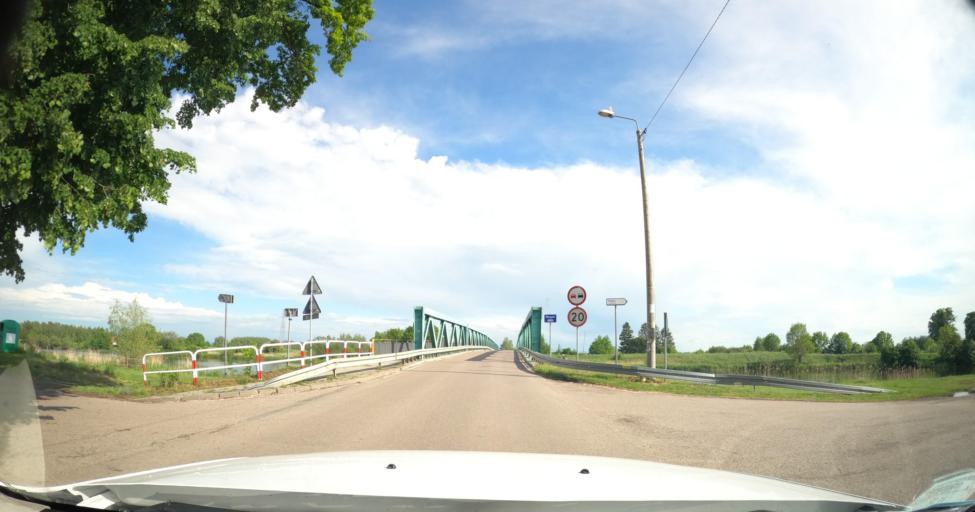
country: PL
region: Warmian-Masurian Voivodeship
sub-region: Powiat elblaski
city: Elblag
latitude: 54.1900
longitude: 19.3138
